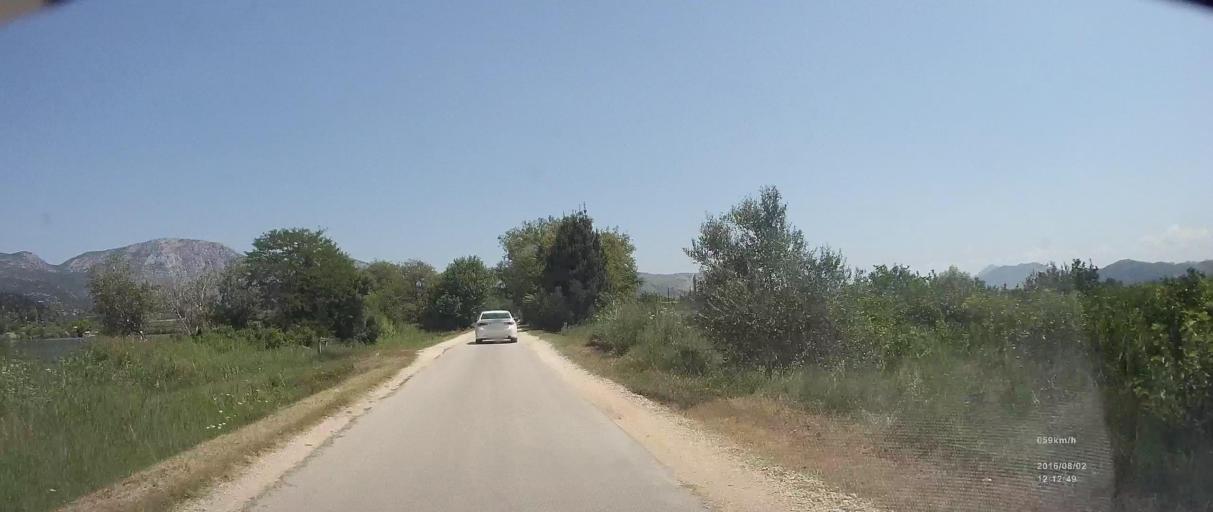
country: HR
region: Dubrovacko-Neretvanska
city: Komin
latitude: 43.0354
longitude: 17.4765
